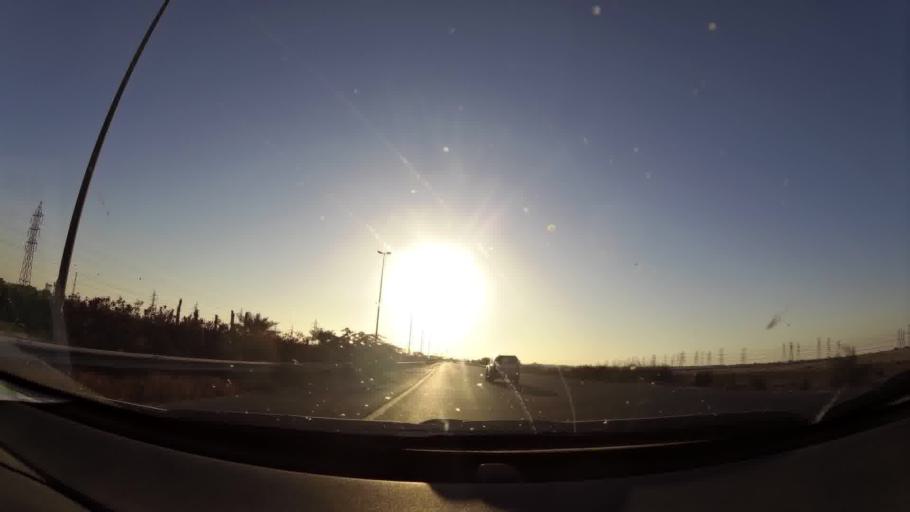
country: KW
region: Al Ahmadi
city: Al Fahahil
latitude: 28.9356
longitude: 48.1897
